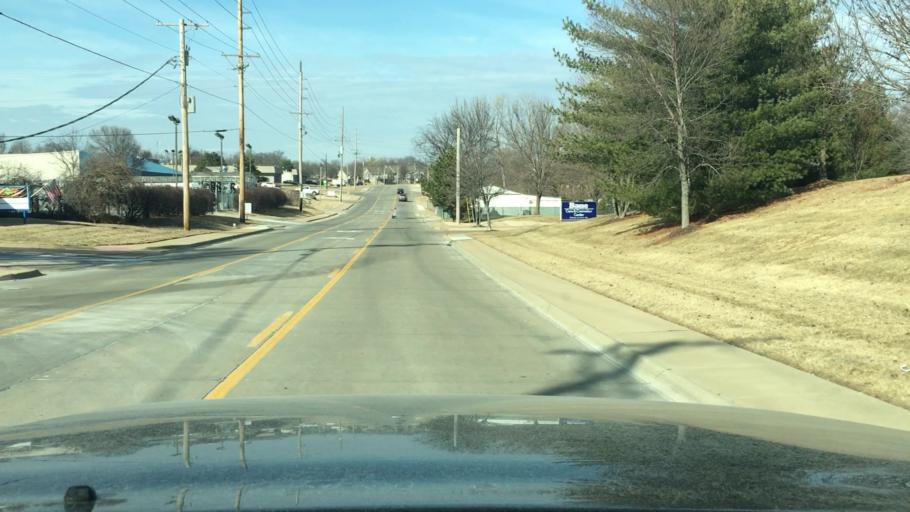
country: US
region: Missouri
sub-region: Saint Charles County
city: Saint Peters
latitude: 38.7972
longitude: -90.5697
